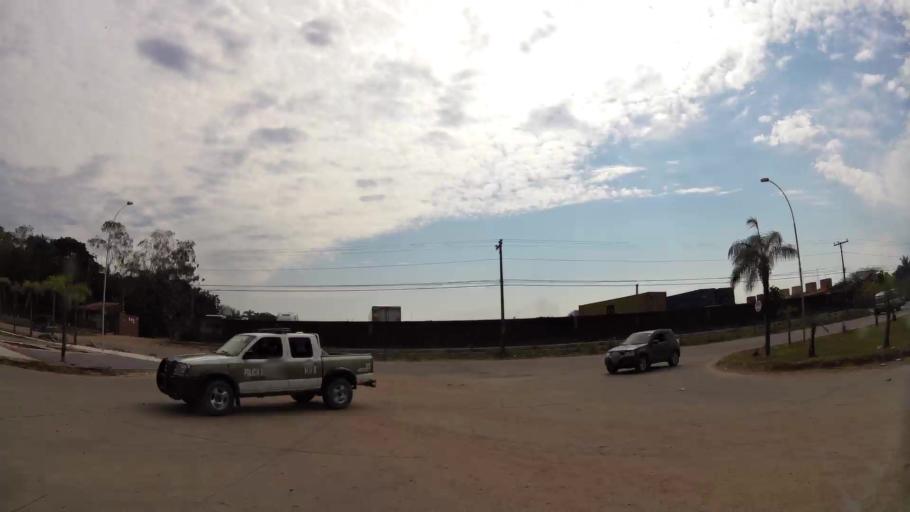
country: BO
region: Santa Cruz
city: Santa Cruz de la Sierra
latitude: -17.7415
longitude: -63.1692
